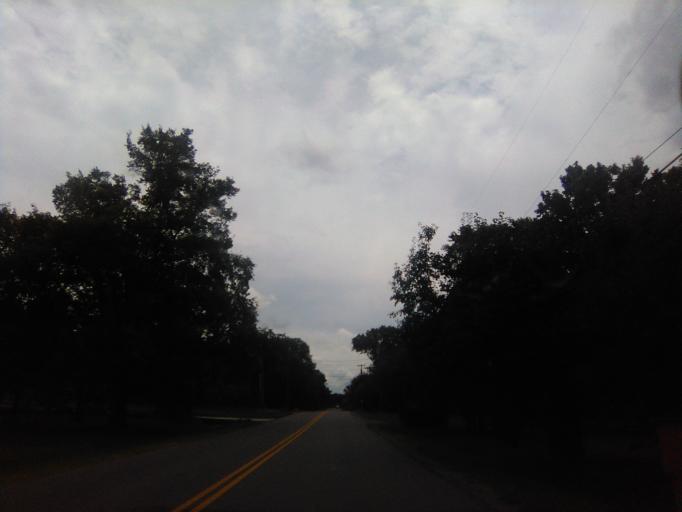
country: US
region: Tennessee
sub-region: Davidson County
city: Belle Meade
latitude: 36.1266
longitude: -86.8917
